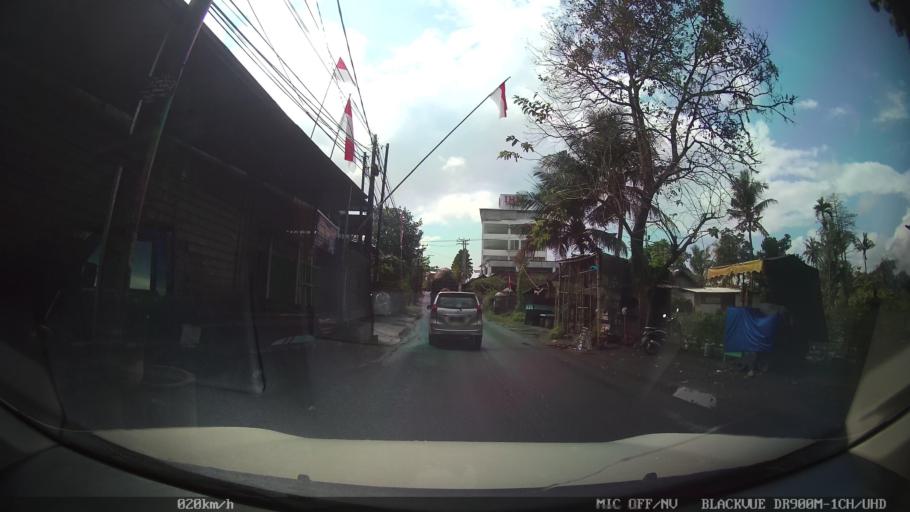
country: ID
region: Bali
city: Banjar Tebongkang
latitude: -8.5418
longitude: 115.2677
